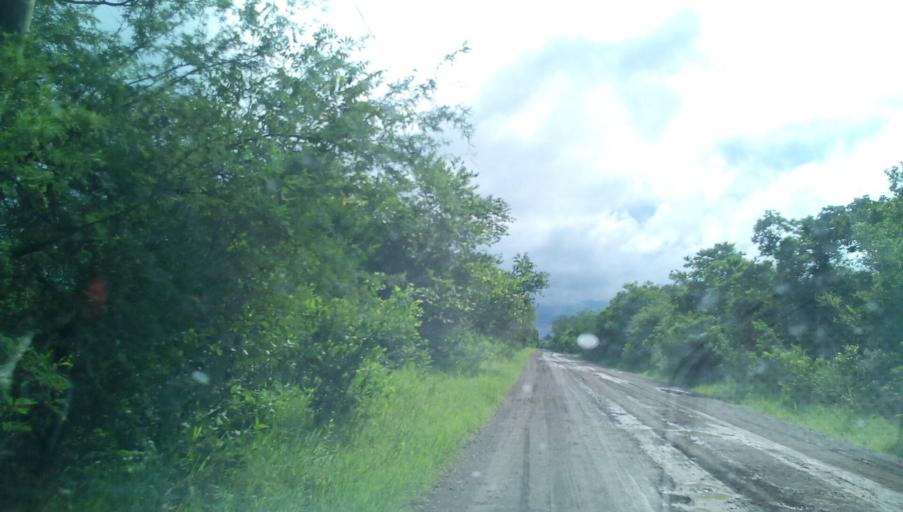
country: MX
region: Veracruz
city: Panuco
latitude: 21.8512
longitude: -98.1642
